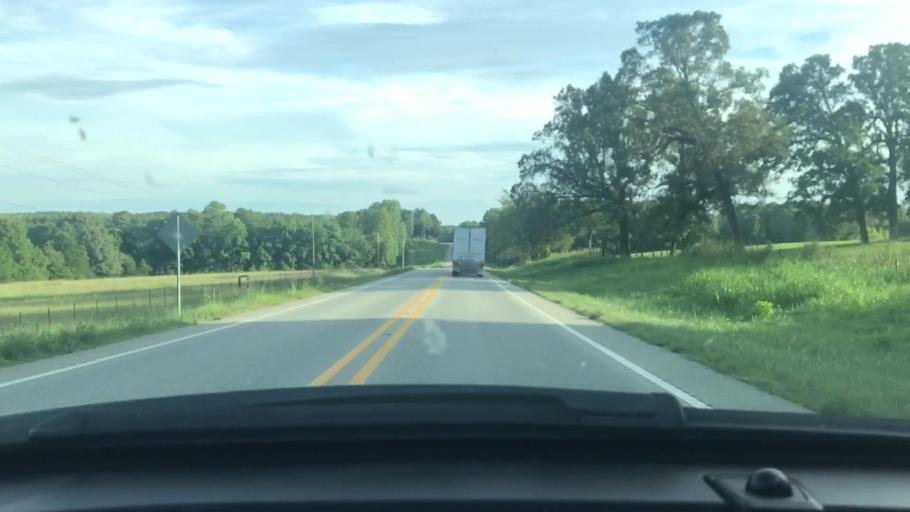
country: US
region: Arkansas
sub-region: Randolph County
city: Pocahontas
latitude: 36.1598
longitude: -91.1620
